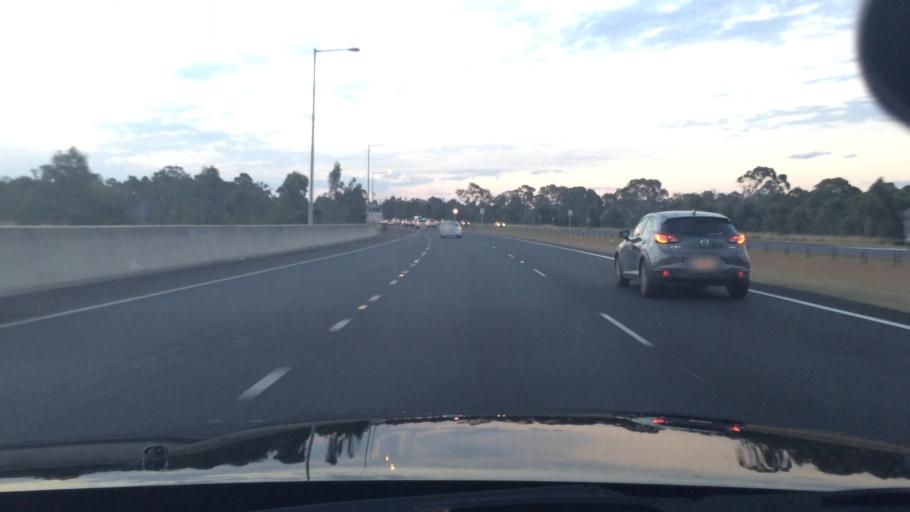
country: AU
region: New South Wales
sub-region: Blacktown
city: Doonside
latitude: -33.7842
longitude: 150.8579
